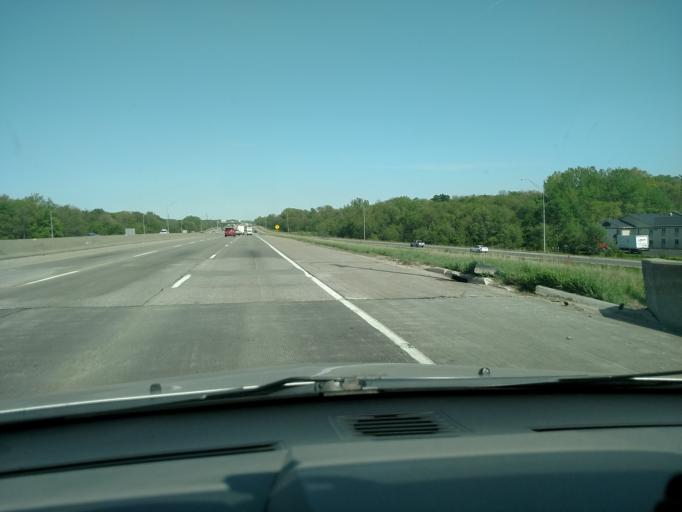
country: US
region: Iowa
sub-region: Polk County
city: Johnston
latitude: 41.6520
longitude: -93.6974
